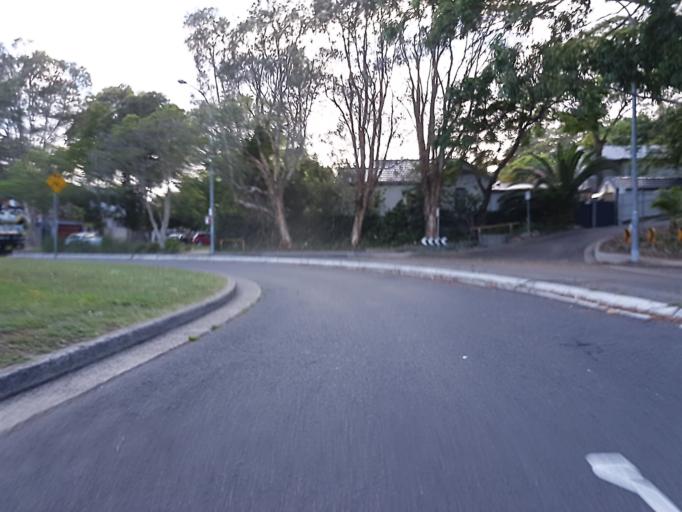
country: AU
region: New South Wales
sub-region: Manly Vale
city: Fairlight
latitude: -33.7896
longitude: 151.2800
